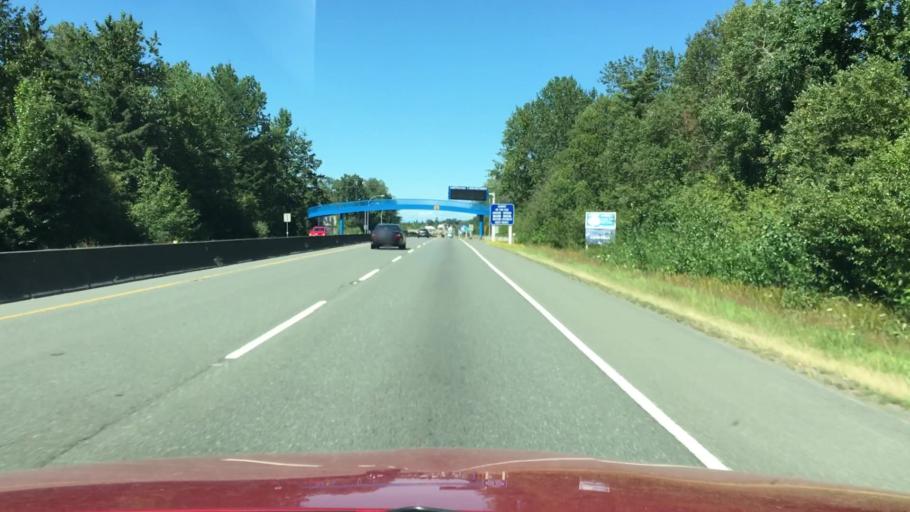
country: CA
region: British Columbia
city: North Saanich
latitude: 48.6395
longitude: -123.4077
